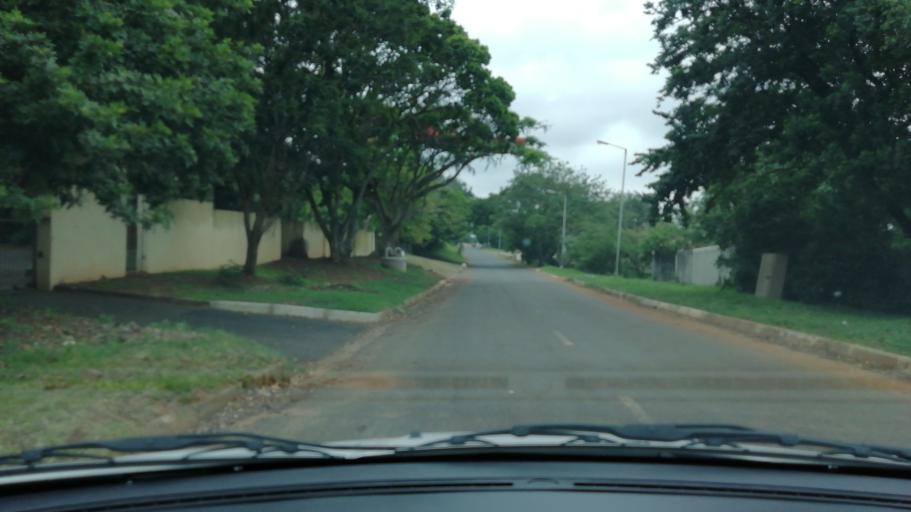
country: ZA
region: KwaZulu-Natal
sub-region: uThungulu District Municipality
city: Empangeni
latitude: -28.7459
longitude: 31.8928
